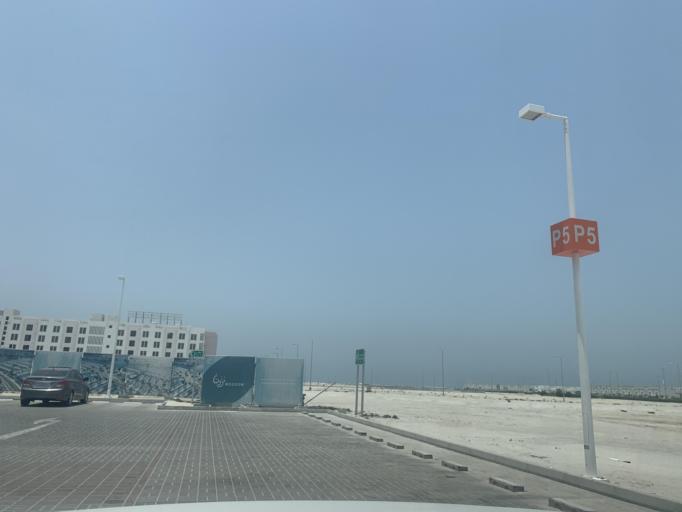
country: BH
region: Muharraq
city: Al Muharraq
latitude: 26.3072
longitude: 50.6239
